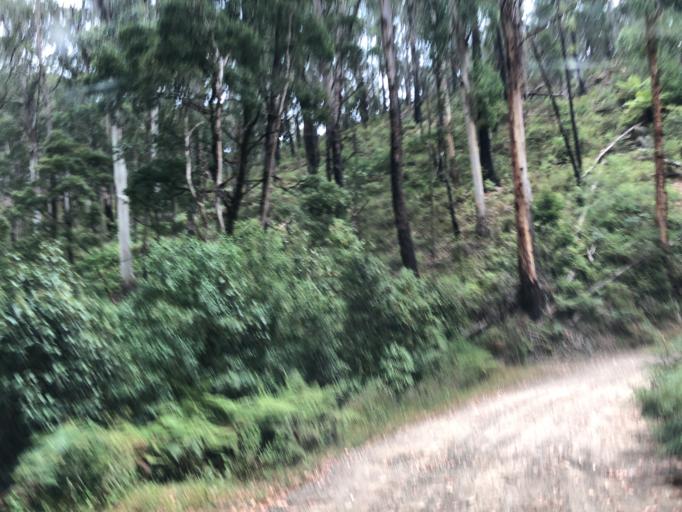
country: AU
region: Victoria
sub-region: Moorabool
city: Bacchus Marsh
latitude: -37.4572
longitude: 144.2685
